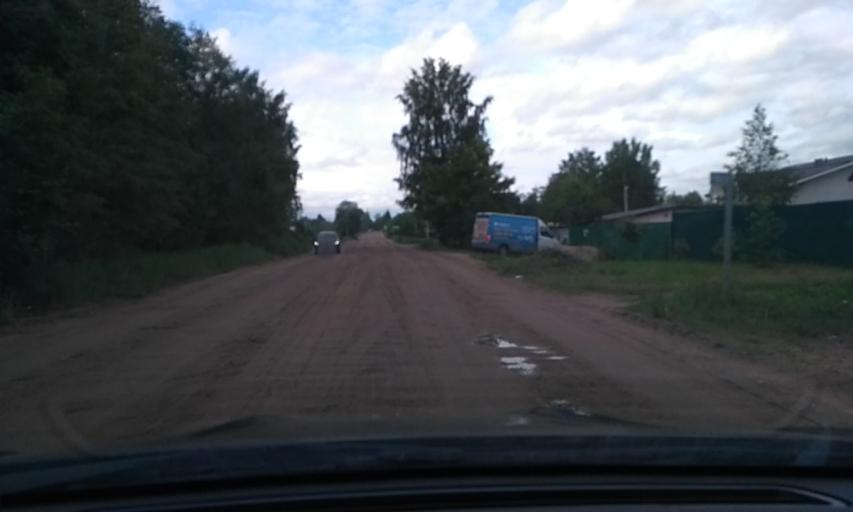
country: RU
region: Leningrad
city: Otradnoye
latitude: 59.7917
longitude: 30.7940
